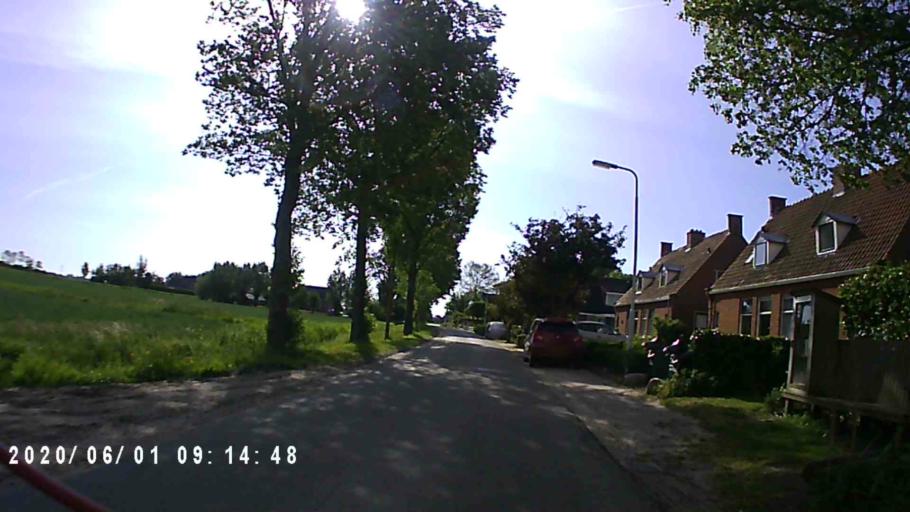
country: NL
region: Friesland
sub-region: Gemeente Leeuwarderadeel
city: Stiens
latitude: 53.2781
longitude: 5.7588
